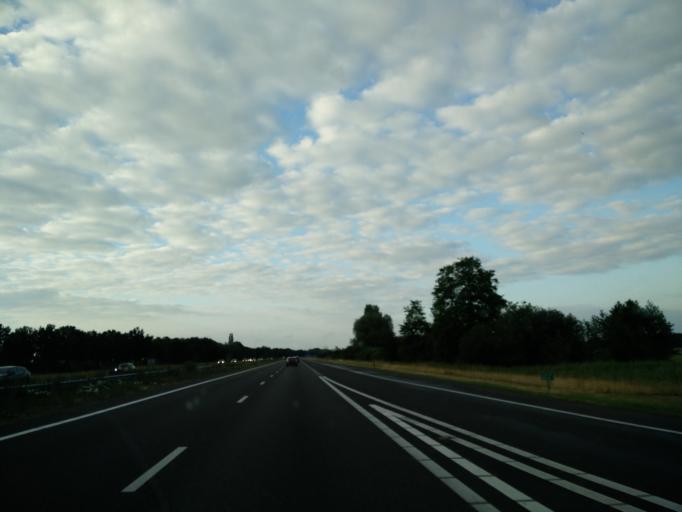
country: NL
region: Gelderland
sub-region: Gemeente Ermelo
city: Horst
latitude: 52.2964
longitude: 5.5529
